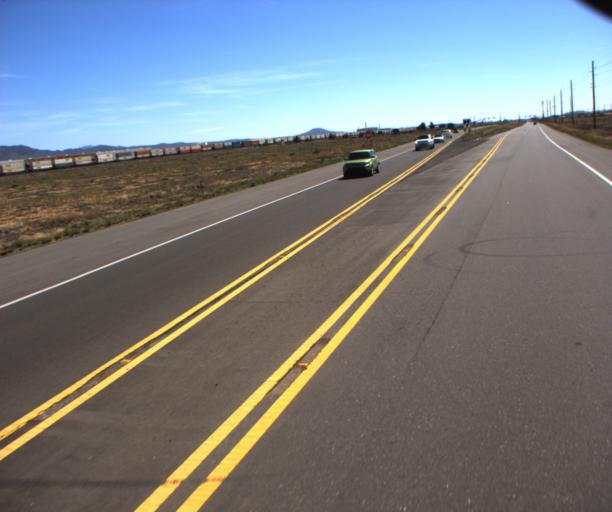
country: US
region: Arizona
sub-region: Mohave County
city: New Kingman-Butler
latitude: 35.2749
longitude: -113.9557
